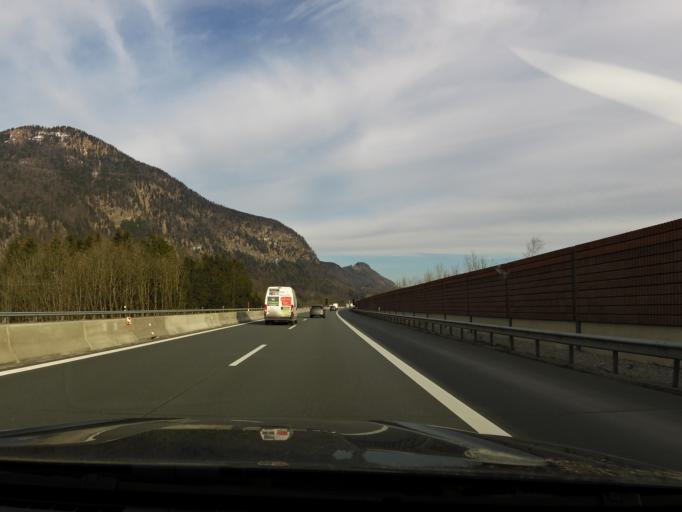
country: AT
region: Tyrol
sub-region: Politischer Bezirk Kufstein
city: Erl
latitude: 47.6731
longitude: 12.1744
